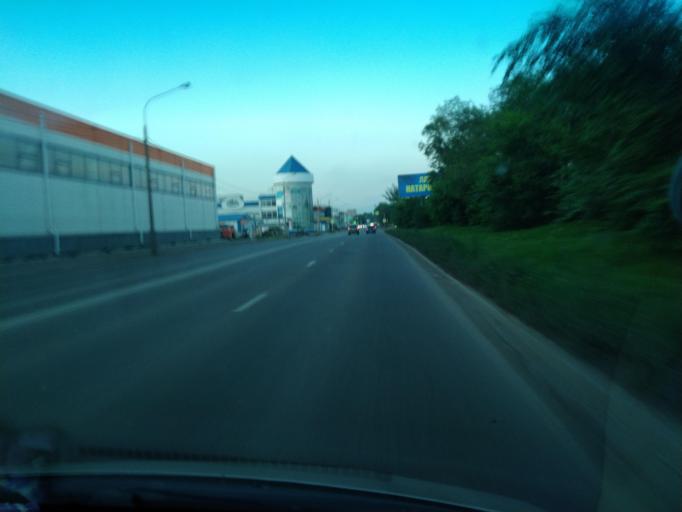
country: RU
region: Krasnoyarskiy
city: Krasnoyarsk
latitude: 55.9908
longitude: 92.9166
